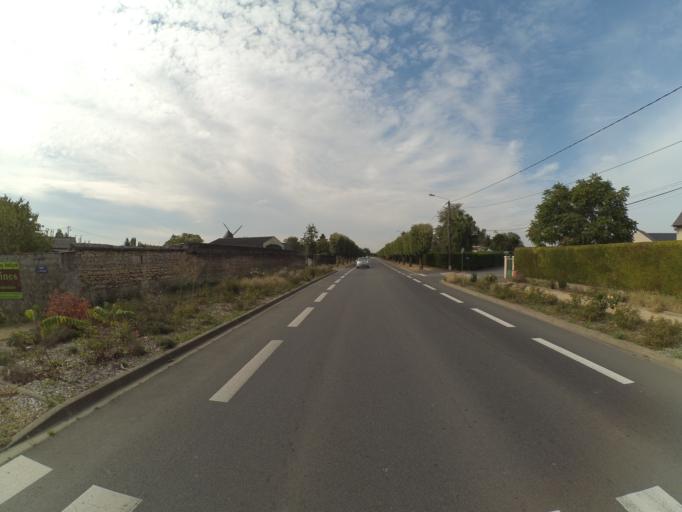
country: FR
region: Pays de la Loire
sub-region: Departement de Maine-et-Loire
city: Doue-la-Fontaine
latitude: 47.1957
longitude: -0.2570
